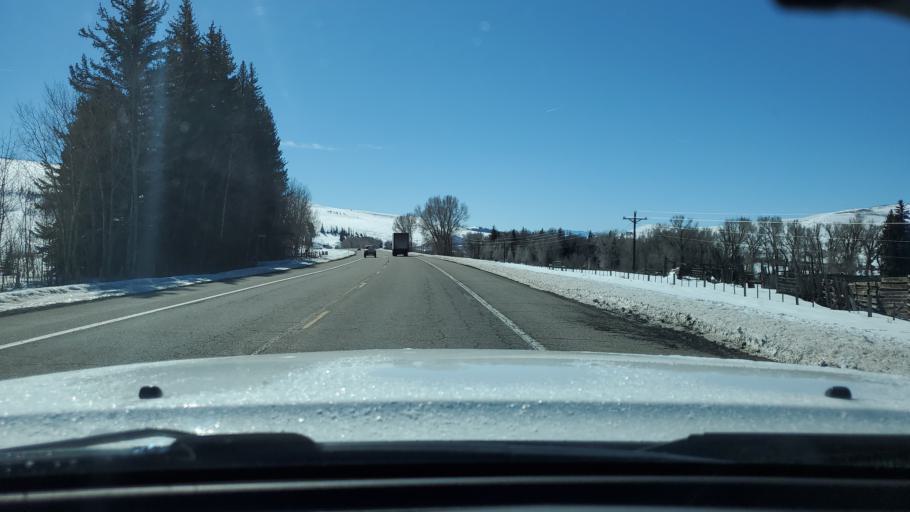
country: US
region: Colorado
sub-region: Gunnison County
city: Crested Butte
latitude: 38.7292
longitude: -106.8510
